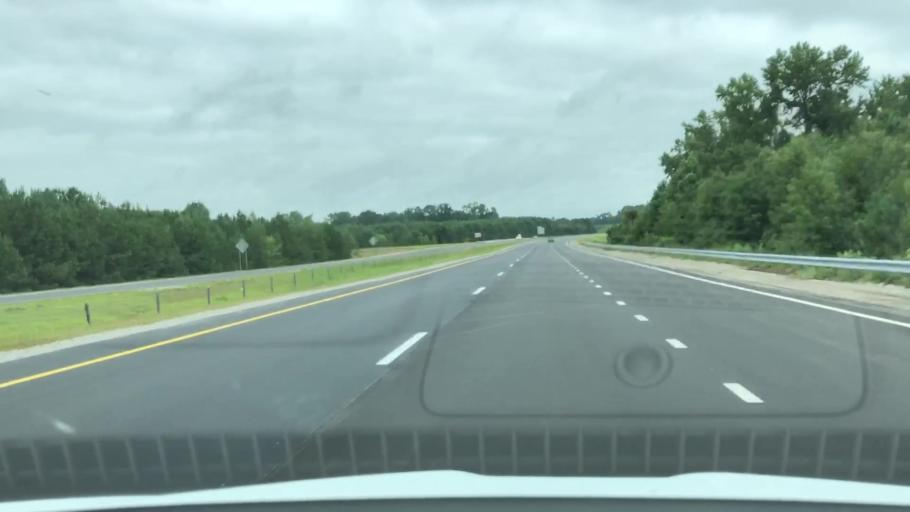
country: US
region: North Carolina
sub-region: Wilson County
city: Lucama
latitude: 35.6708
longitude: -77.9586
